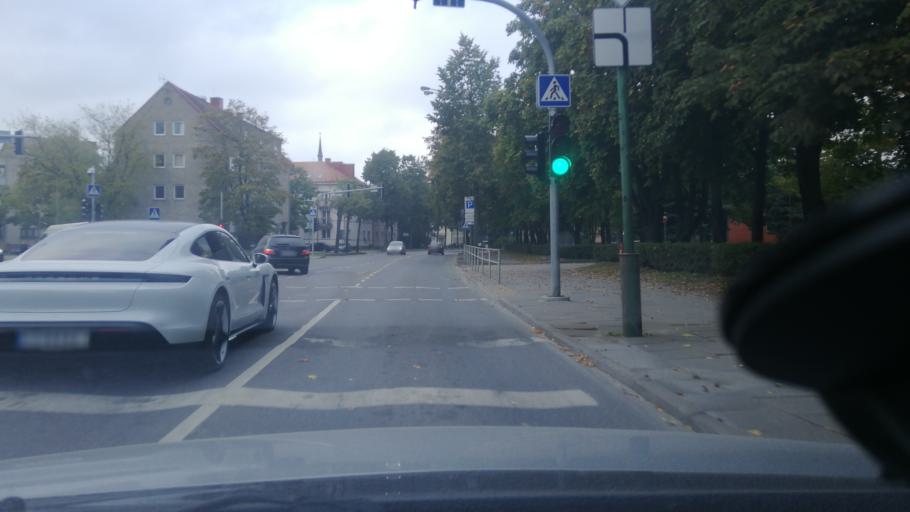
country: LT
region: Klaipedos apskritis
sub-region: Klaipeda
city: Klaipeda
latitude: 55.7045
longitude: 21.1527
